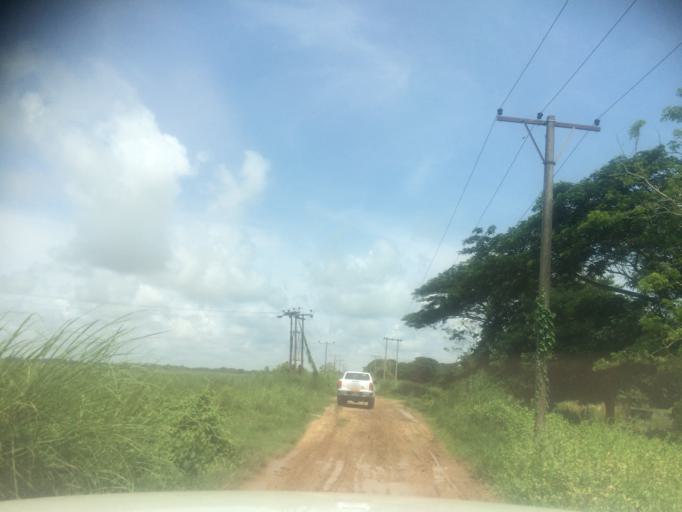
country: MM
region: Bago
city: Tharyarwady
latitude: 17.3175
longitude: 95.8972
